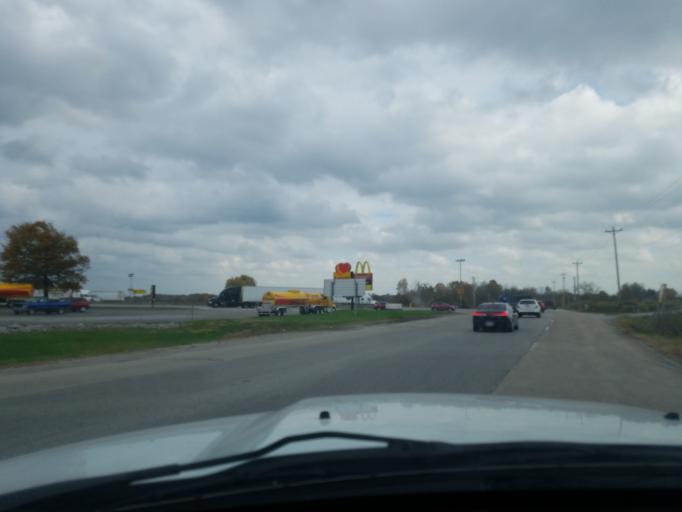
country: US
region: Indiana
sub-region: Clark County
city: Henryville
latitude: 38.4896
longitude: -85.7706
